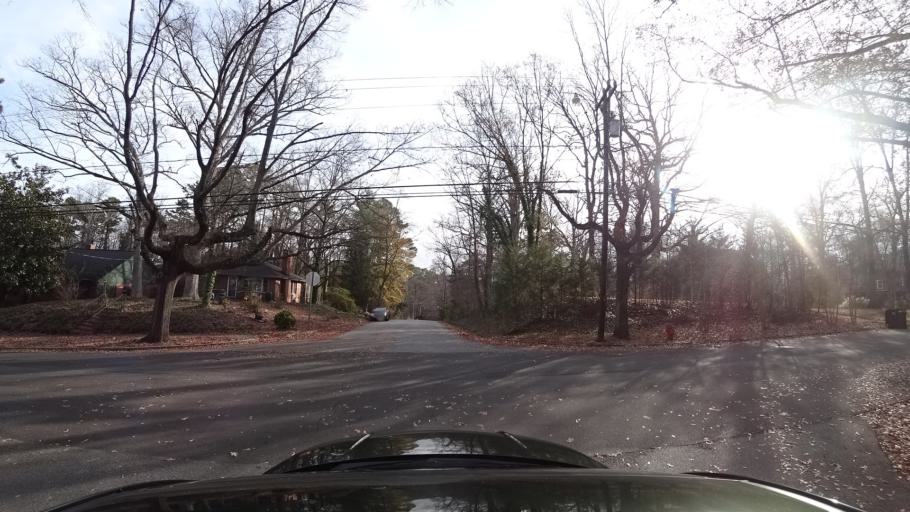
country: US
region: North Carolina
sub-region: Durham County
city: Durham
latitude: 36.0146
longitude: -78.8961
